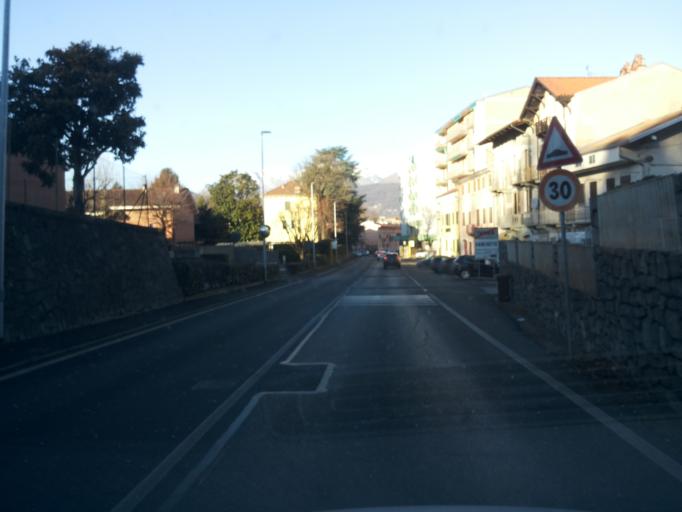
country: IT
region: Piedmont
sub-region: Provincia di Torino
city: Banchette
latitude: 45.4595
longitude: 7.8632
